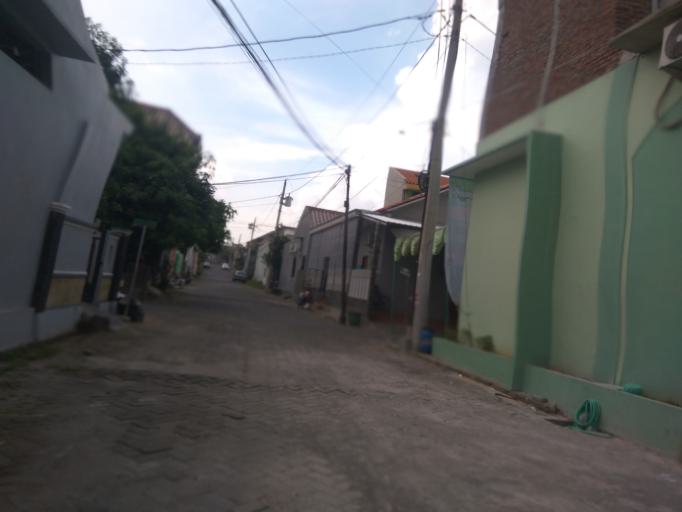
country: ID
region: Central Java
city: Semarang
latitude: -7.0655
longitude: 110.4460
